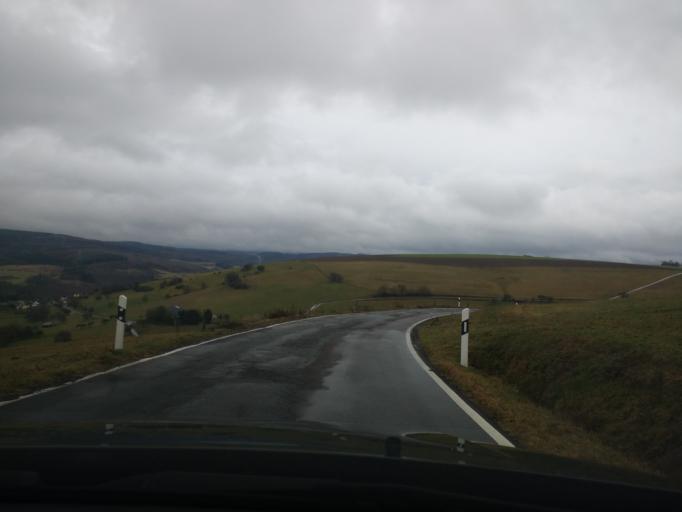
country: DE
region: Rheinland-Pfalz
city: Franzenheim
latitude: 49.6769
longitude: 6.6990
